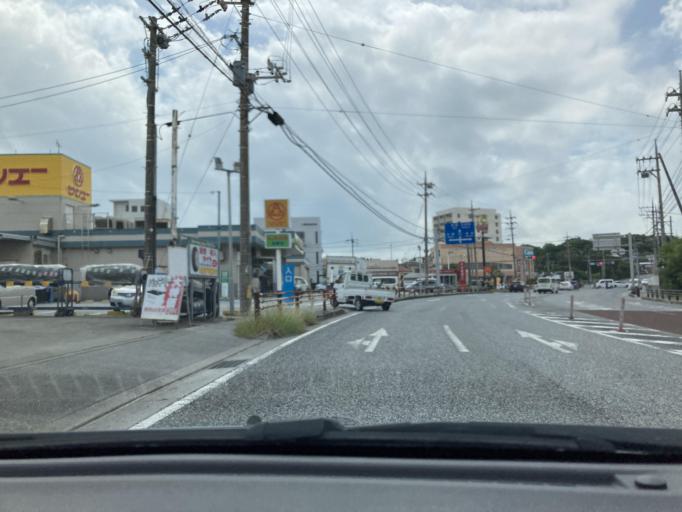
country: JP
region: Okinawa
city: Okinawa
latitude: 26.3193
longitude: 127.8213
